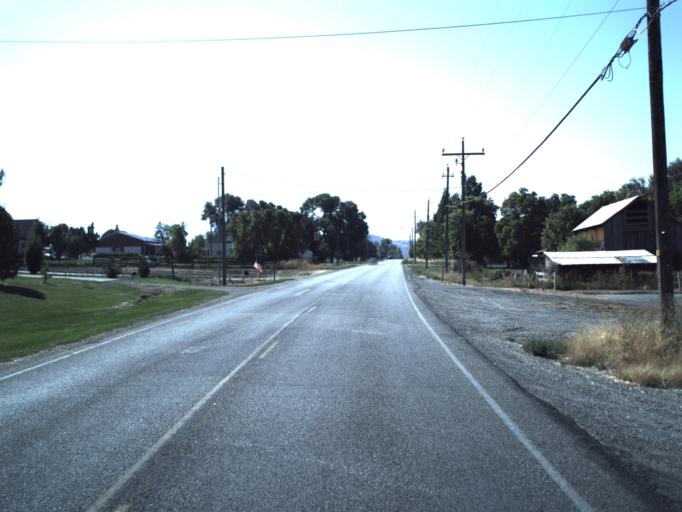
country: US
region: Utah
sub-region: Cache County
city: Hyrum
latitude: 41.5747
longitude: -111.8383
